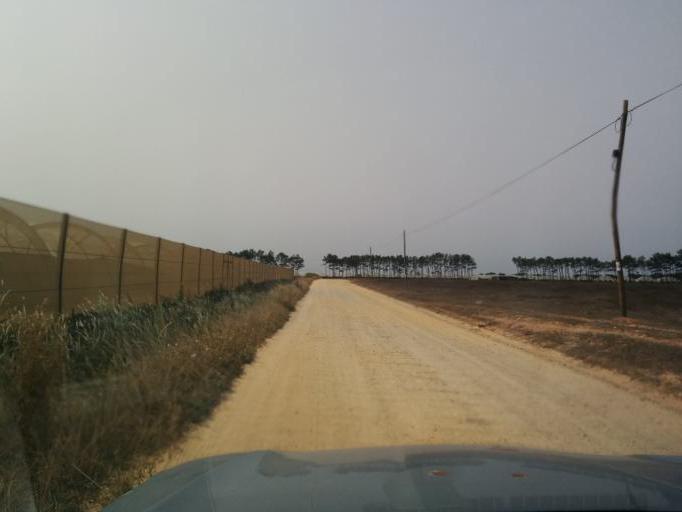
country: PT
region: Beja
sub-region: Odemira
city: Sao Teotonio
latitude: 37.5112
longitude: -8.7840
